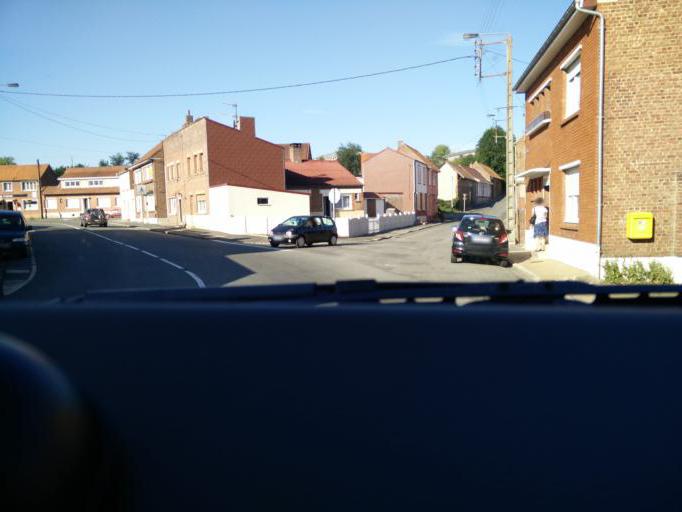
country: FR
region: Nord-Pas-de-Calais
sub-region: Departement du Pas-de-Calais
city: Divion
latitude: 50.4560
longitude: 2.4812
